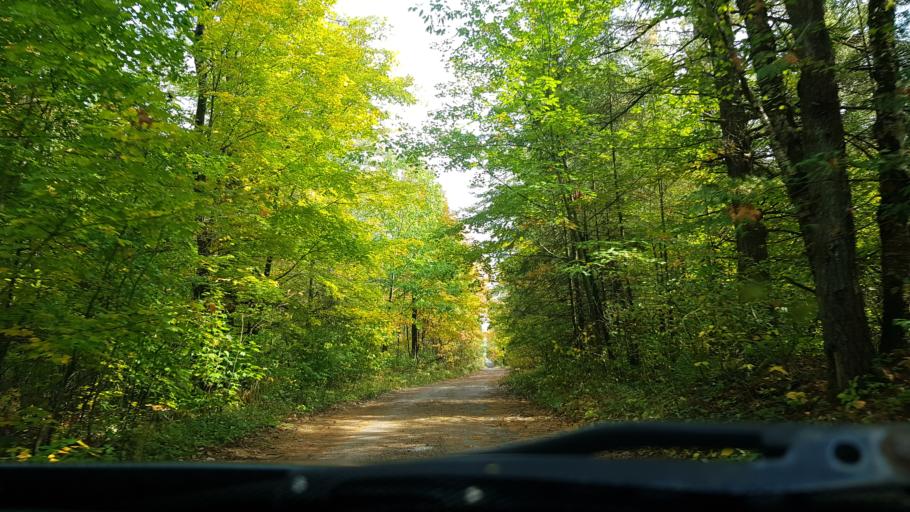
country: CA
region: Ontario
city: Orillia
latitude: 44.6823
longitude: -79.0620
